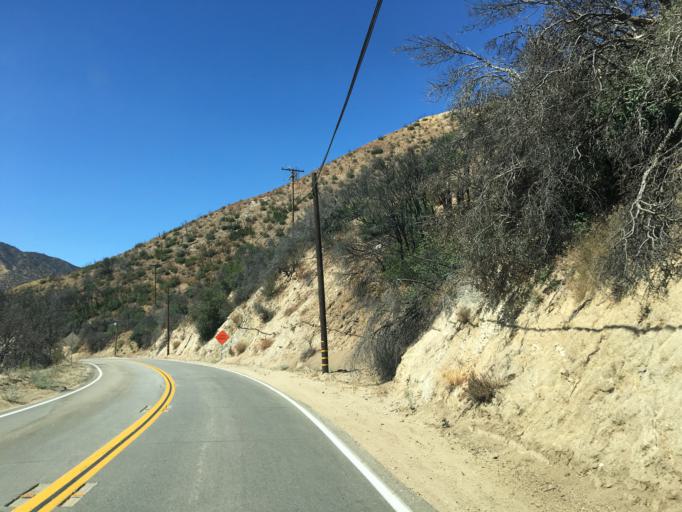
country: US
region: California
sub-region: Los Angeles County
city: Green Valley
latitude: 34.6687
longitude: -118.4548
